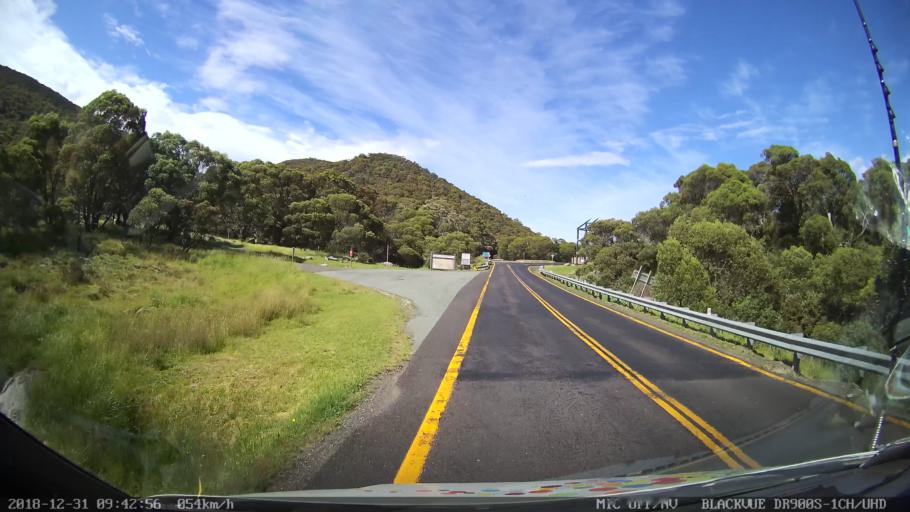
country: AU
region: New South Wales
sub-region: Snowy River
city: Jindabyne
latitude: -36.4994
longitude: 148.3179
